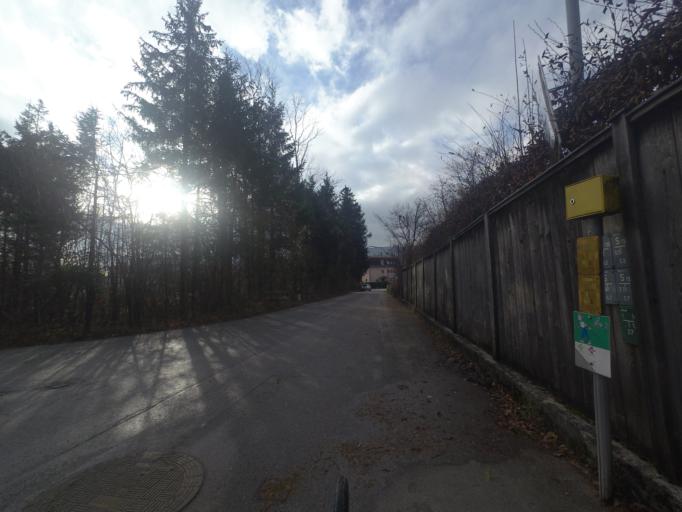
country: AT
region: Salzburg
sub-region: Politischer Bezirk Salzburg-Umgebung
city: Anif
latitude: 47.7276
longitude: 13.0702
